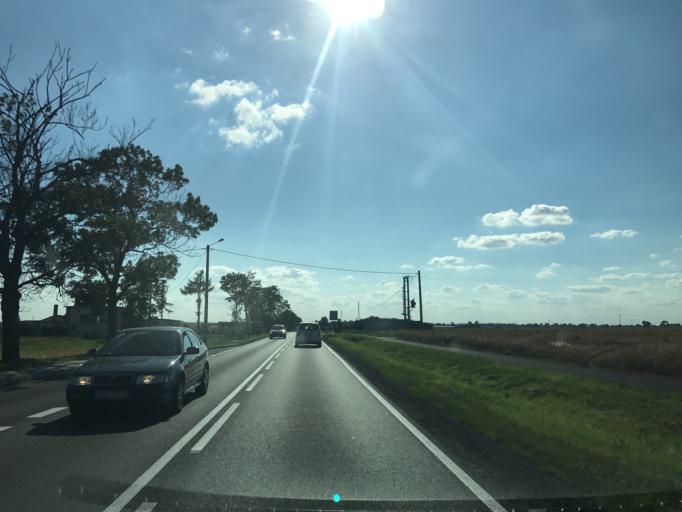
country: PL
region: Kujawsko-Pomorskie
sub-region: Powiat wloclawski
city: Brzesc Kujawski
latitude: 52.6177
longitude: 18.9483
